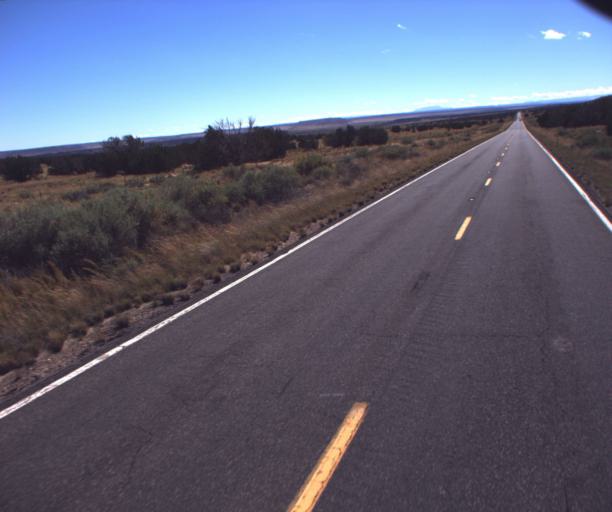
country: US
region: Arizona
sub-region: Apache County
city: Saint Johns
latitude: 34.8058
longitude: -109.2379
